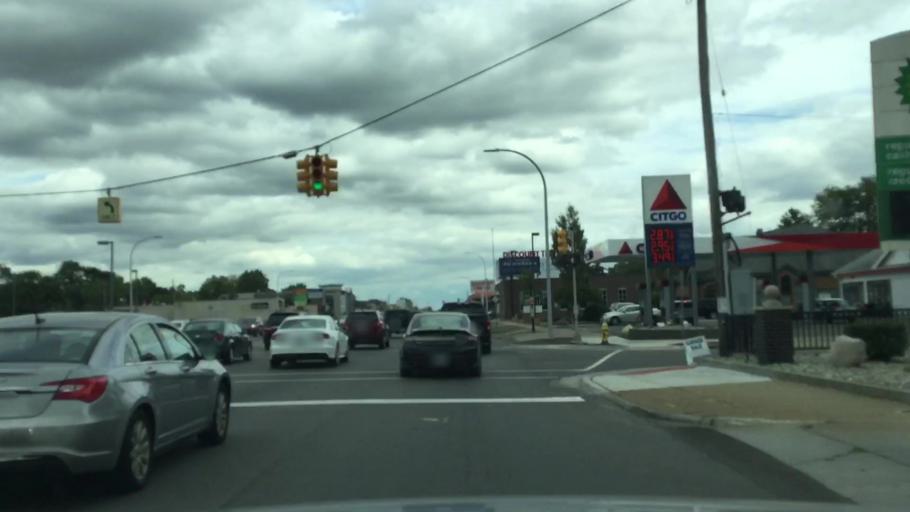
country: US
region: Michigan
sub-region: Wayne County
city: Dearborn Heights
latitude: 42.3266
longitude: -83.2874
